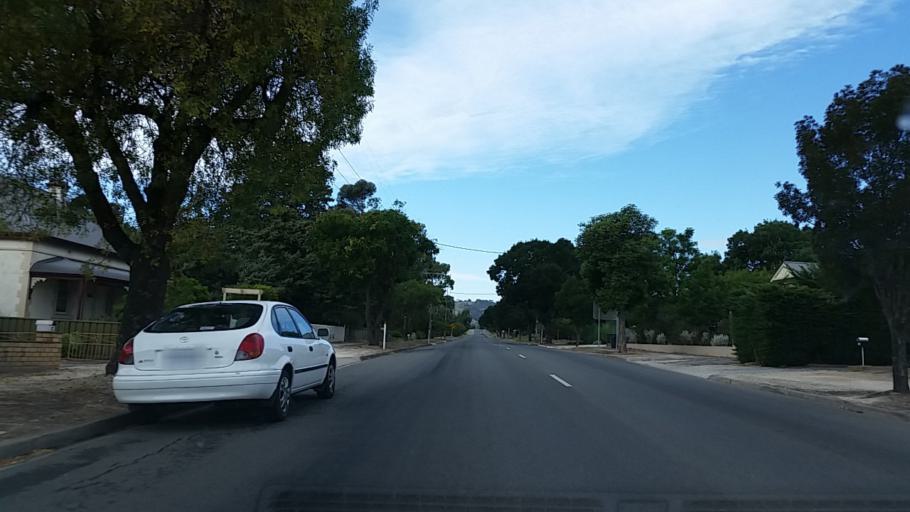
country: AU
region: South Australia
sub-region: Barossa
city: Tanunda
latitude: -34.5328
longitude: 138.9523
